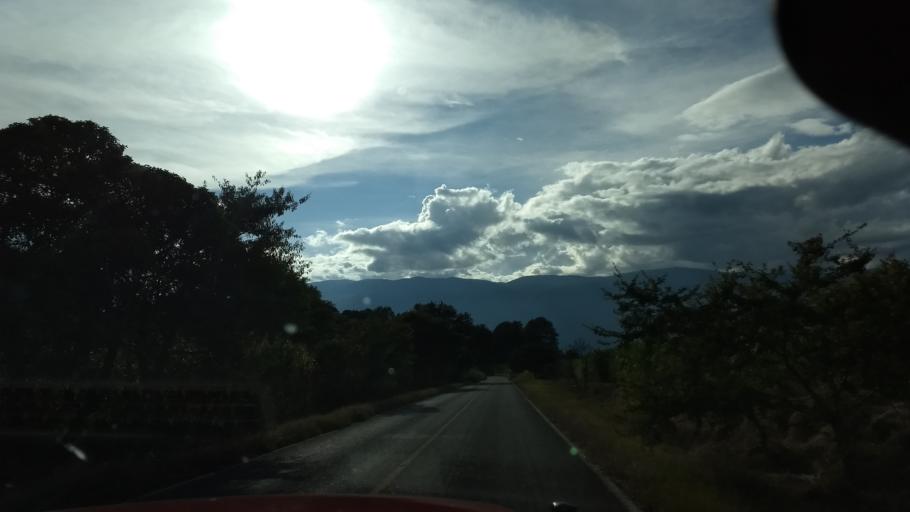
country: MX
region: Colima
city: Suchitlan
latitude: 19.4674
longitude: -103.7683
